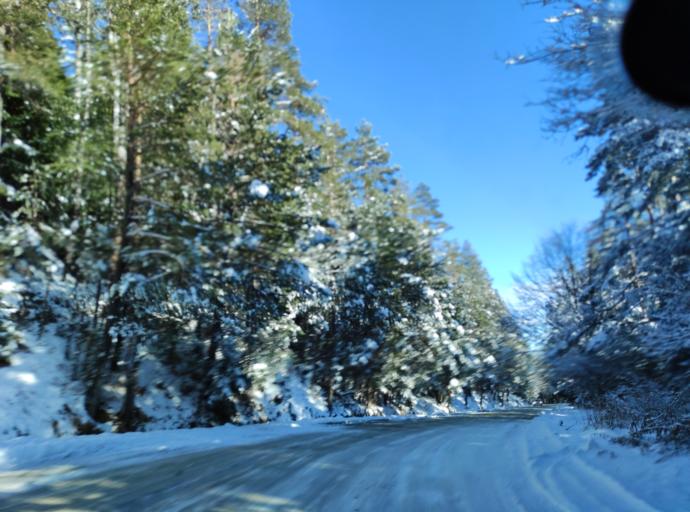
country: BG
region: Sofia-Capital
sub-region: Stolichna Obshtina
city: Sofia
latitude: 42.5891
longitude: 23.2990
